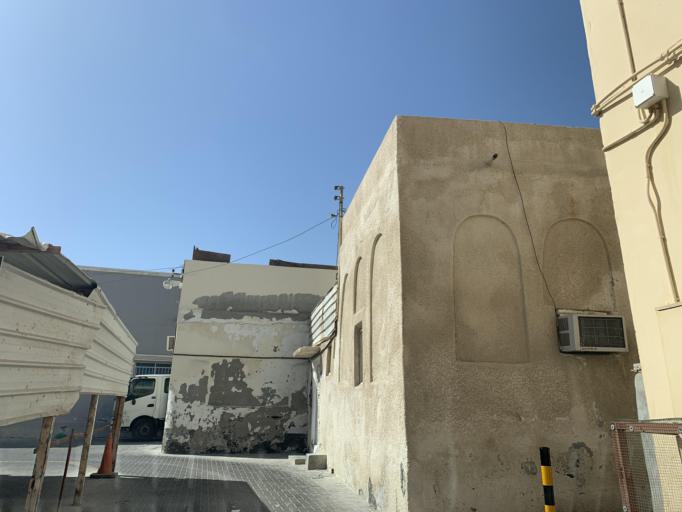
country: BH
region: Muharraq
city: Al Muharraq
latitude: 26.2589
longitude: 50.6102
